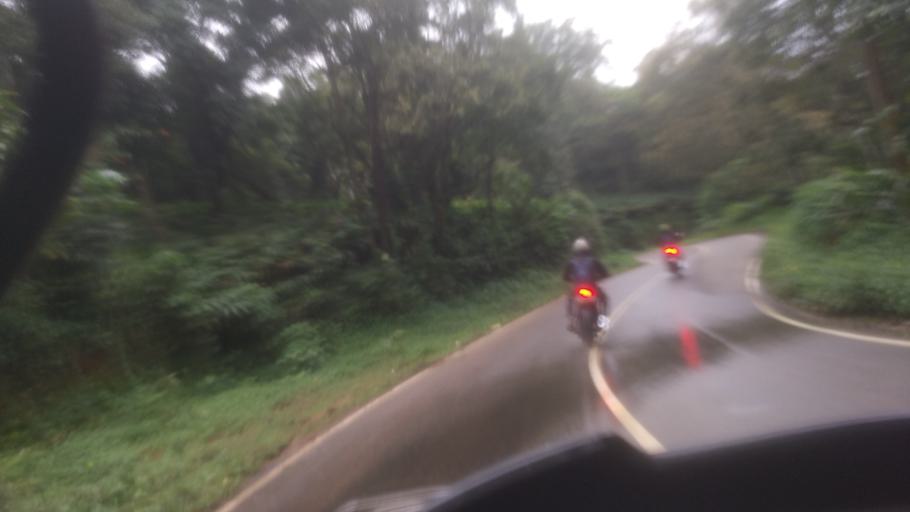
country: IN
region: Tamil Nadu
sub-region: Theni
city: Kombai
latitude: 9.8929
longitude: 77.2001
